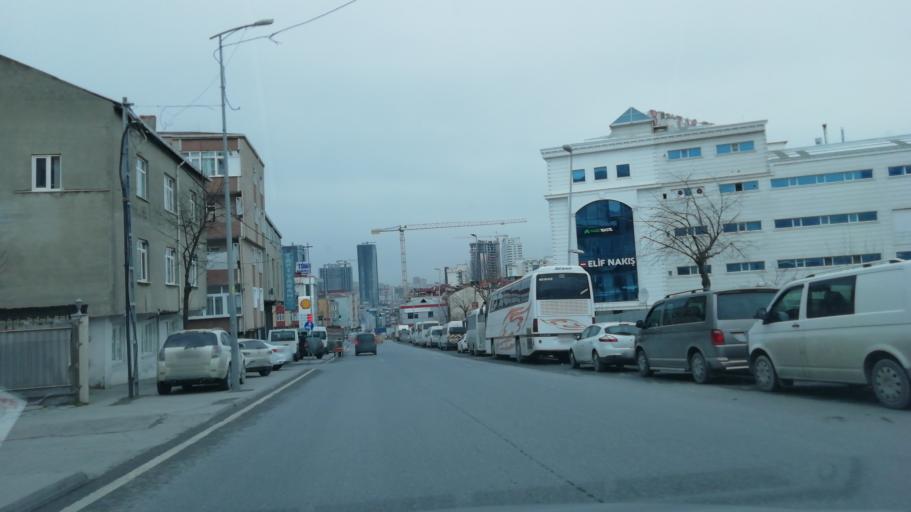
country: TR
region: Istanbul
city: Mahmutbey
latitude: 41.0452
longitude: 28.8219
